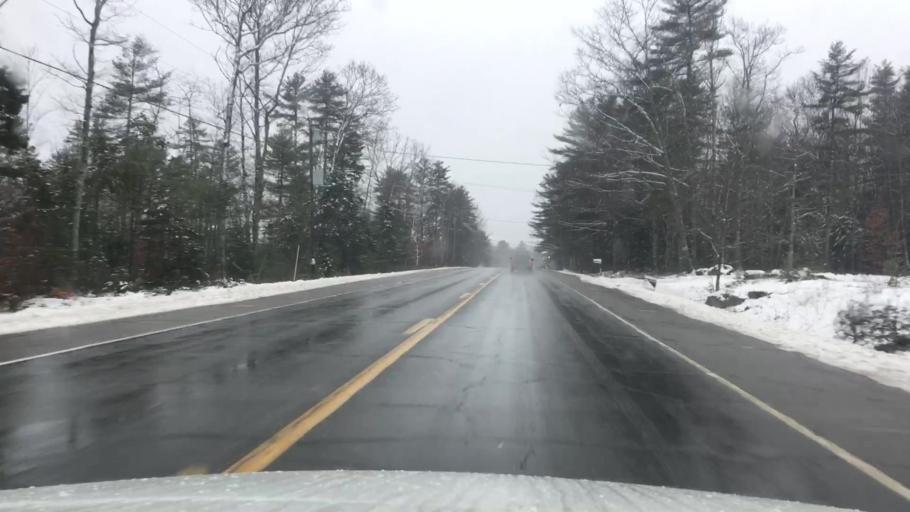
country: US
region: Maine
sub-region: Knox County
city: Warren
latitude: 44.1560
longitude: -69.1840
